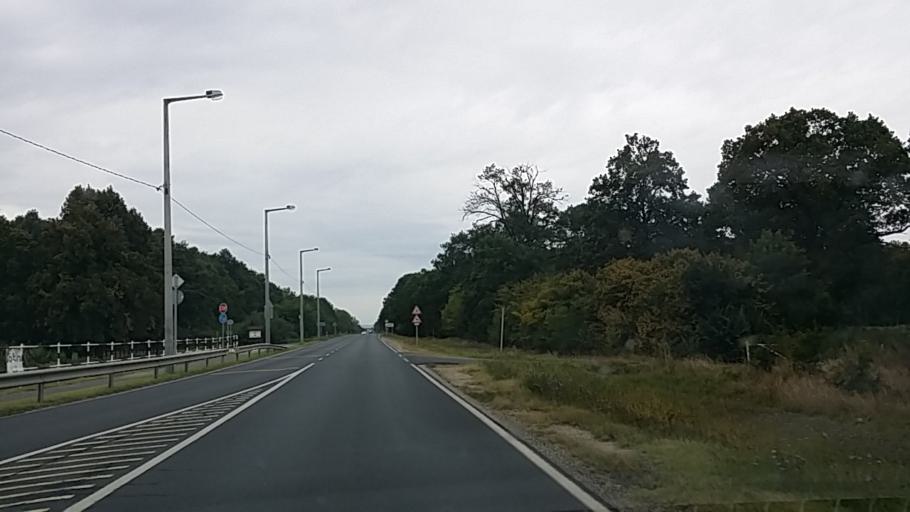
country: HU
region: Gyor-Moson-Sopron
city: Kapuvar
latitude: 47.5871
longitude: 16.9746
